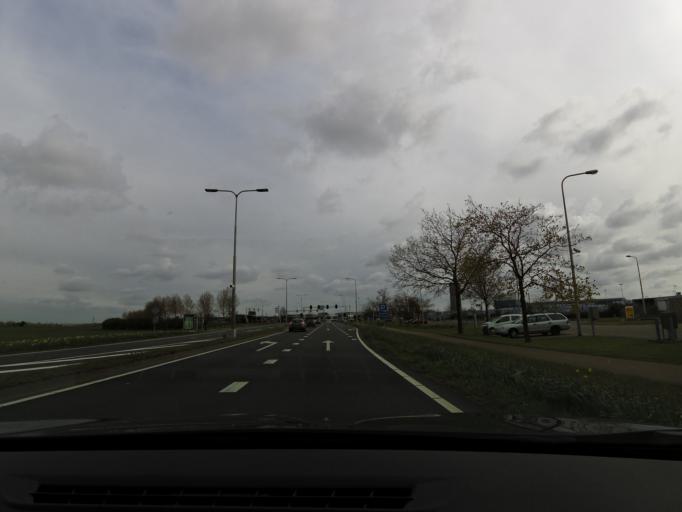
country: NL
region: South Holland
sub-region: Gemeente Hillegom
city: Hillegom
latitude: 52.2780
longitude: 4.5713
